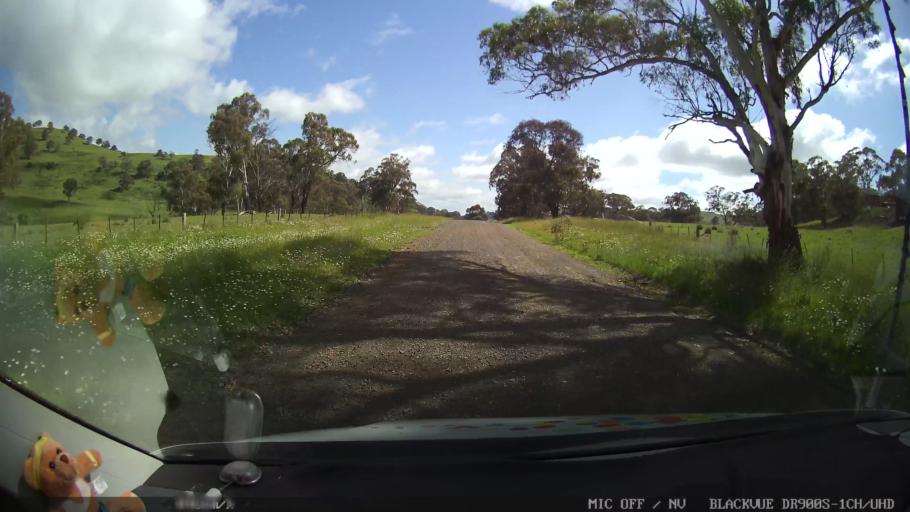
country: AU
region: New South Wales
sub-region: Guyra
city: Guyra
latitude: -29.9899
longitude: 151.6882
